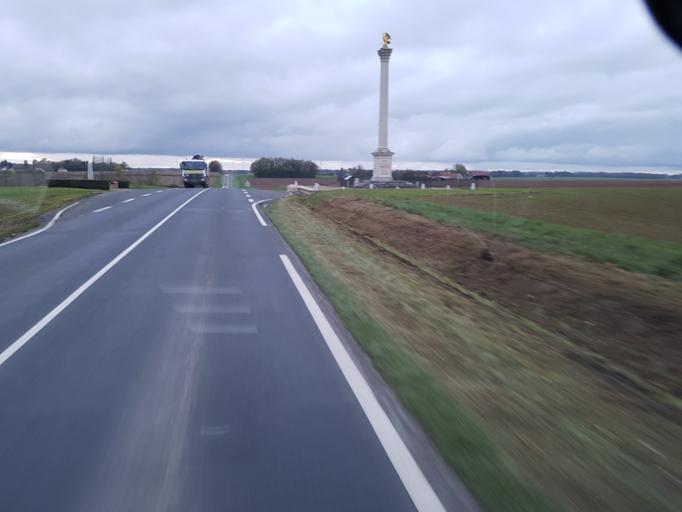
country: FR
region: Champagne-Ardenne
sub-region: Departement de la Marne
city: Montmirail
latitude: 48.8854
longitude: 3.5094
